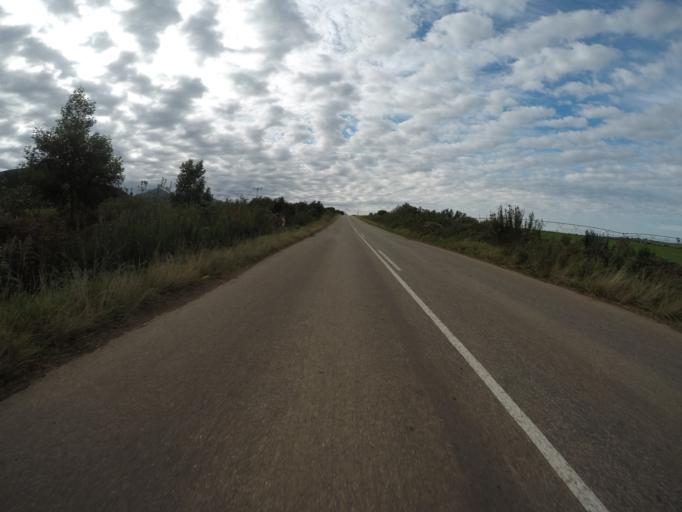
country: ZA
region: Eastern Cape
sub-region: Cacadu District Municipality
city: Kareedouw
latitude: -34.0102
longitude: 24.2777
